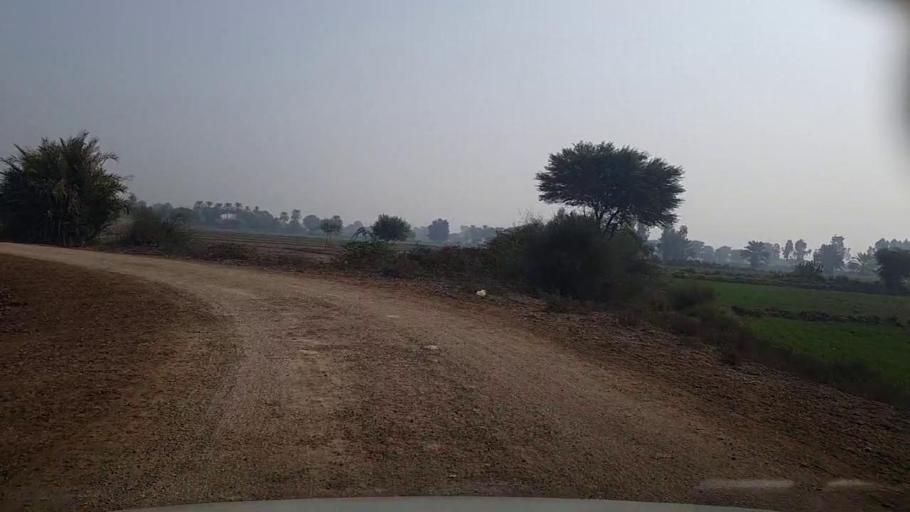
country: PK
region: Sindh
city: Setharja Old
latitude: 27.1430
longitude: 68.4914
